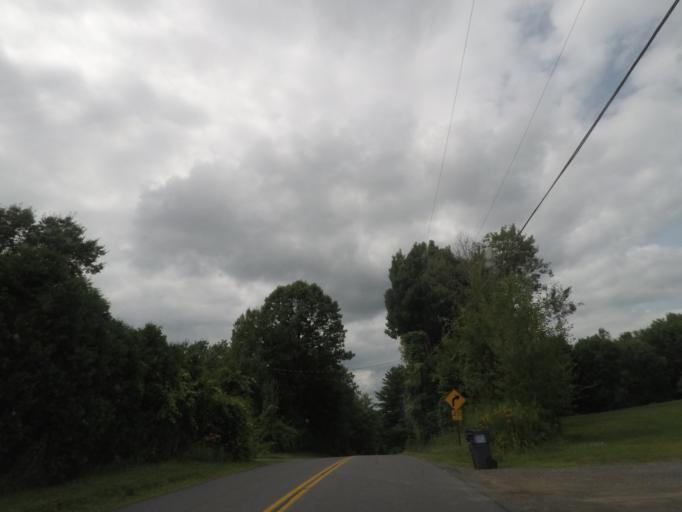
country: US
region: New York
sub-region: Saratoga County
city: Stillwater
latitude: 43.0011
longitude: -73.6950
